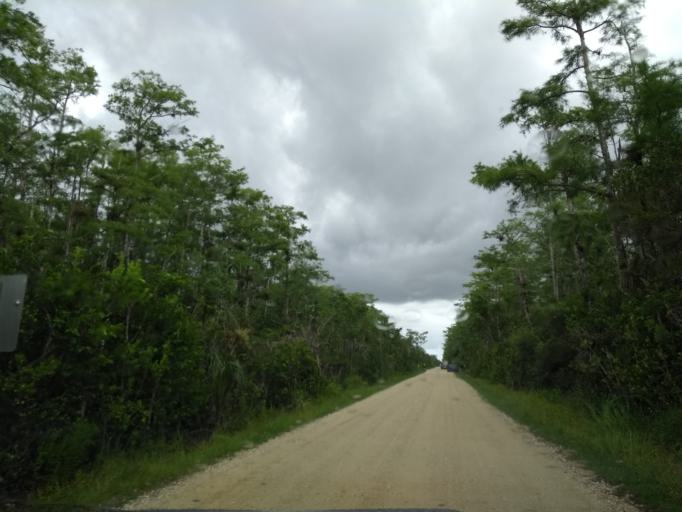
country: US
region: Florida
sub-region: Miami-Dade County
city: The Hammocks
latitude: 25.7472
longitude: -80.9559
